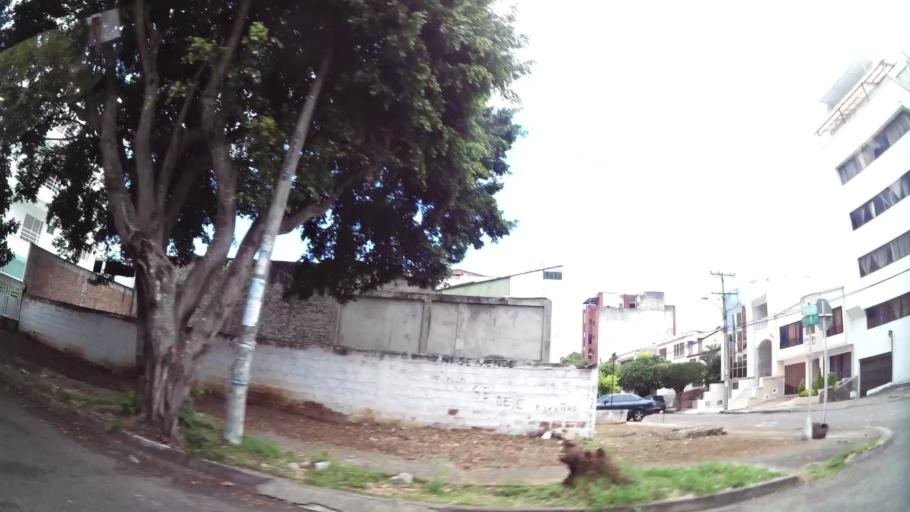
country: CO
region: Valle del Cauca
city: Cali
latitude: 3.3835
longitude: -76.5277
